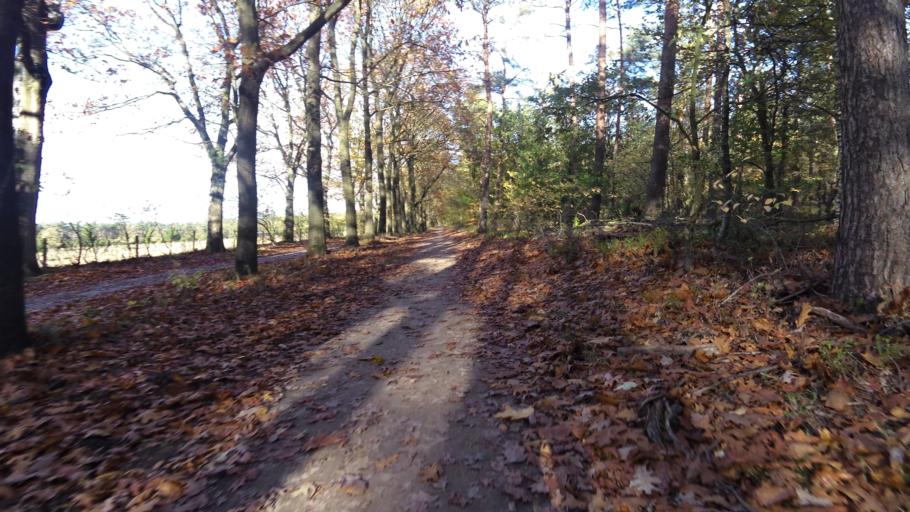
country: NL
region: Gelderland
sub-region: Gemeente Heerde
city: Heerde
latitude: 52.3960
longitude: 5.9977
